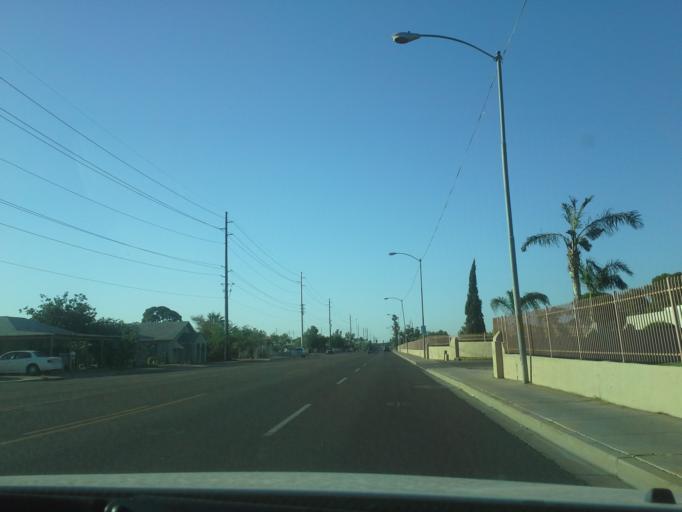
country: US
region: Arizona
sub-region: Maricopa County
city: Phoenix
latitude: 33.4545
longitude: -112.1174
